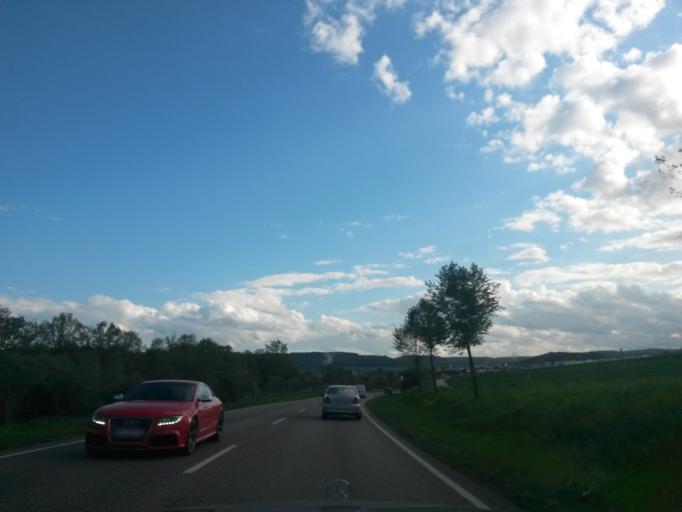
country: DE
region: Baden-Wuerttemberg
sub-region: Regierungsbezirk Stuttgart
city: Aalen
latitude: 48.8456
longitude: 10.0700
